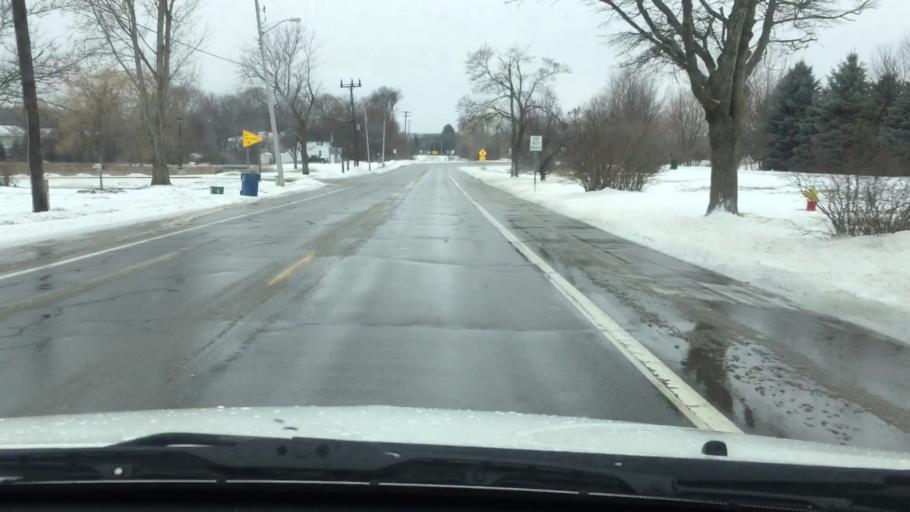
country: US
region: Michigan
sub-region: Wexford County
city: Cadillac
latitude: 44.2355
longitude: -85.4126
